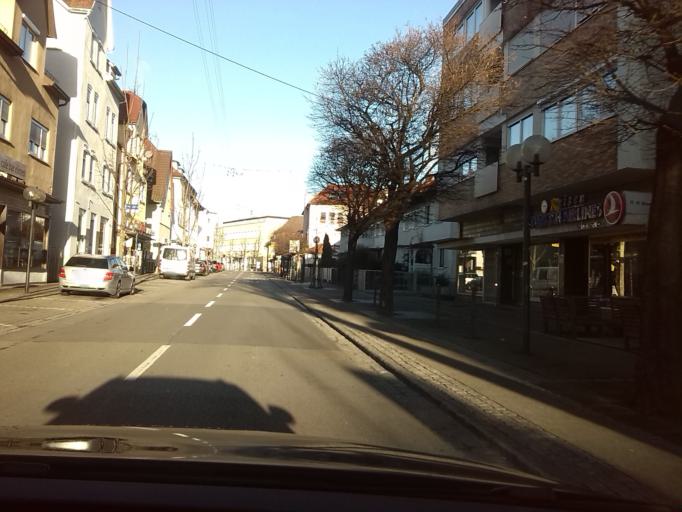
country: DE
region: Baden-Wuerttemberg
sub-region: Regierungsbezirk Stuttgart
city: Fellbach
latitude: 48.8134
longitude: 9.2759
